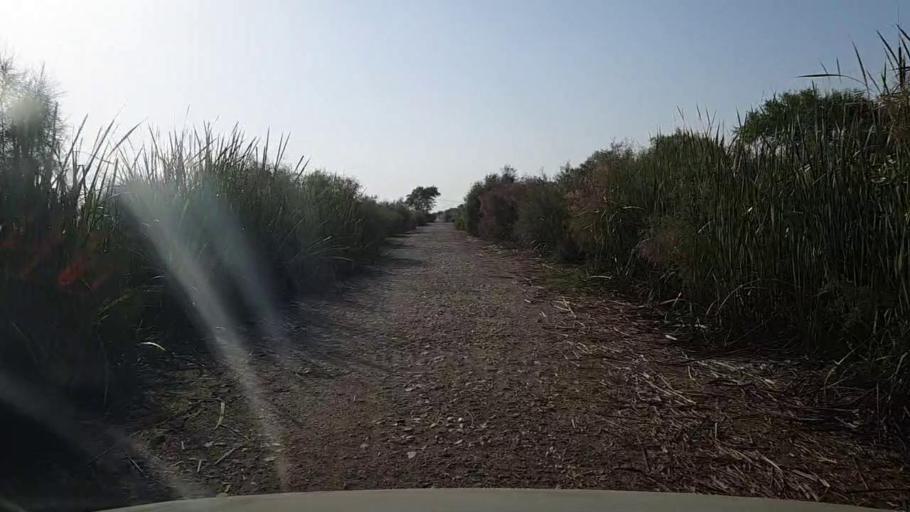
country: PK
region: Sindh
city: Kandhkot
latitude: 28.2895
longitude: 69.3272
